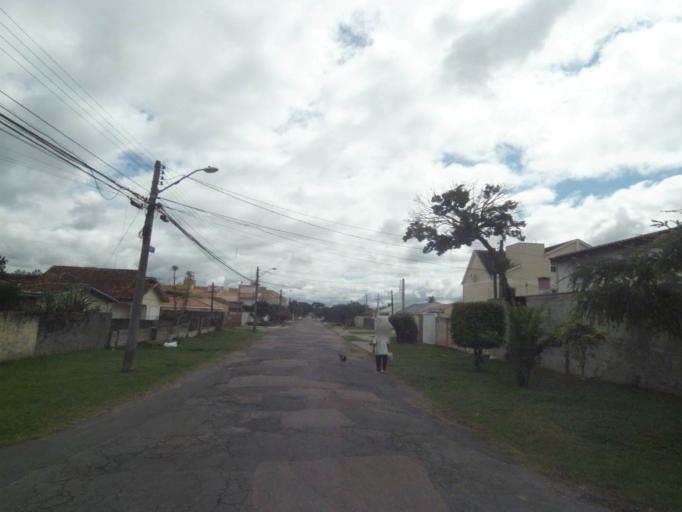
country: BR
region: Parana
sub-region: Curitiba
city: Curitiba
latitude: -25.4783
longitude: -49.2683
